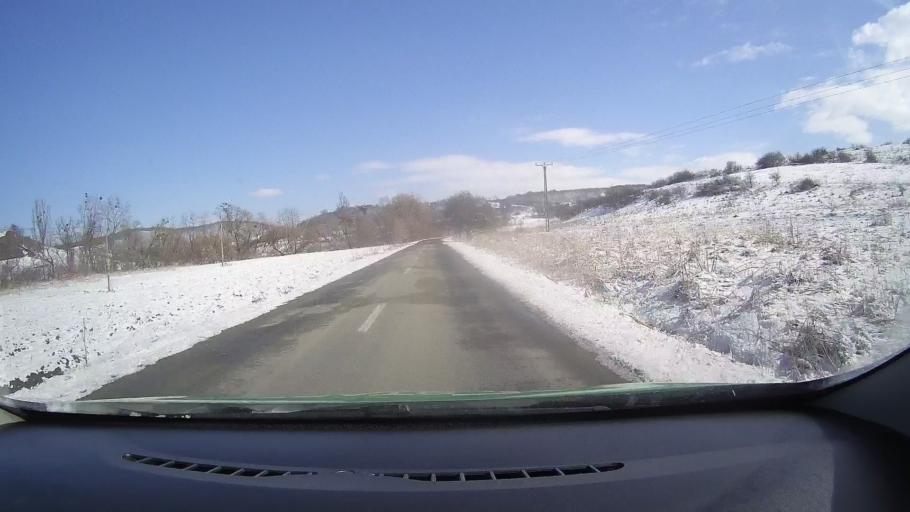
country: RO
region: Sibiu
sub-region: Comuna Mihaileni
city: Mihaileni
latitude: 46.0158
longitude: 24.3802
